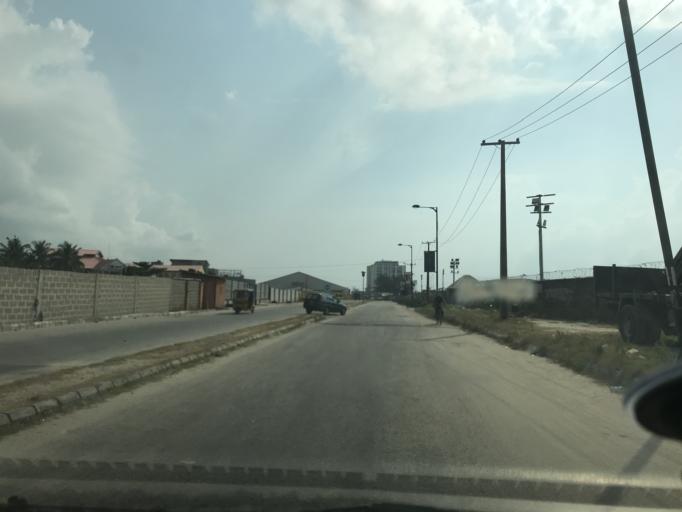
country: NG
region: Lagos
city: Ikoyi
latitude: 6.4245
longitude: 3.4416
